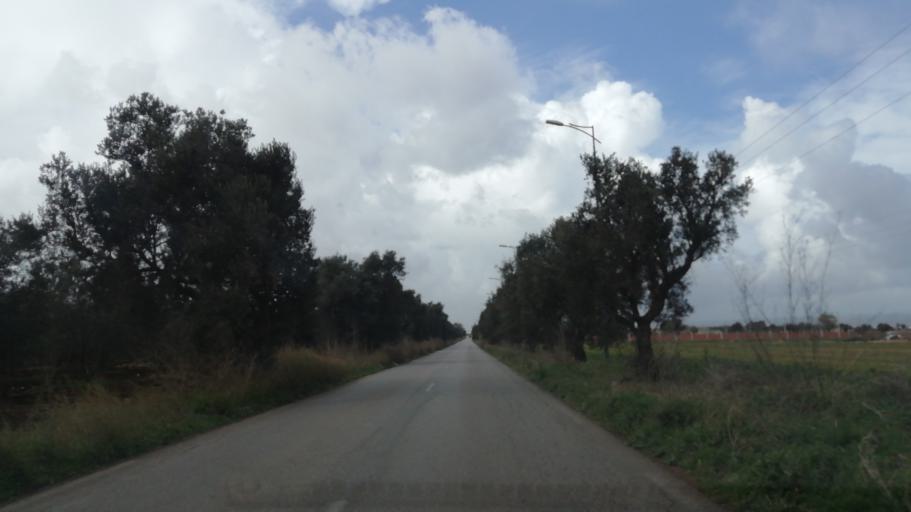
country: DZ
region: Oran
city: Sidi ech Chahmi
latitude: 35.6225
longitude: -0.5589
